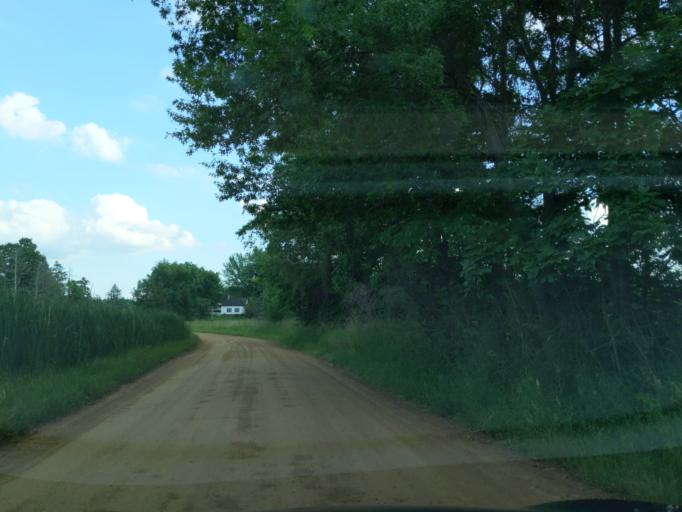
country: US
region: Michigan
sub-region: Shiawassee County
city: Laingsburg
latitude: 42.8314
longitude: -84.3700
